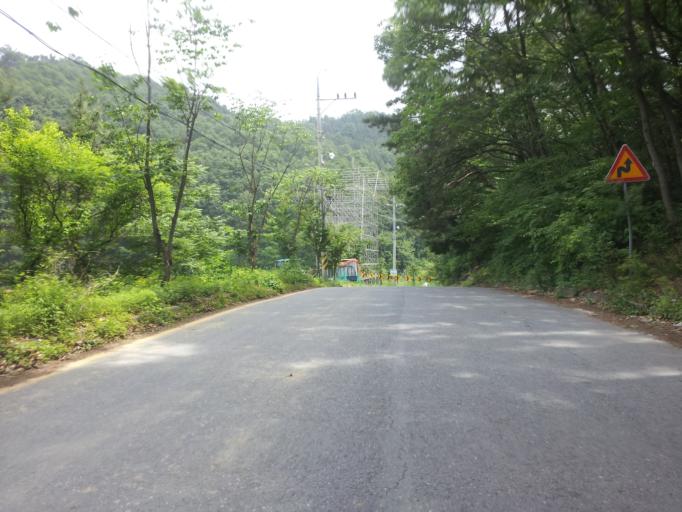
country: KR
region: Daejeon
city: Daejeon
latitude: 36.3317
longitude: 127.4876
